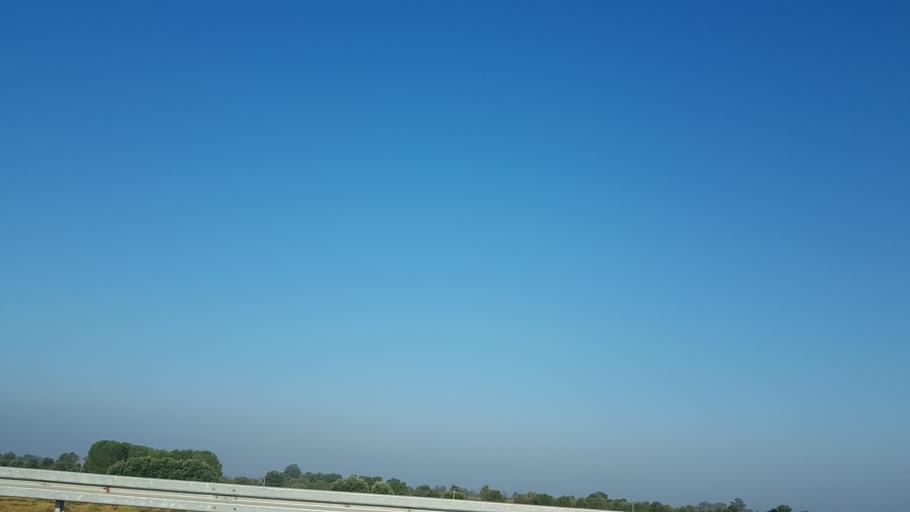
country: TR
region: Bursa
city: Tatkavakli
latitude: 40.1121
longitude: 28.2771
